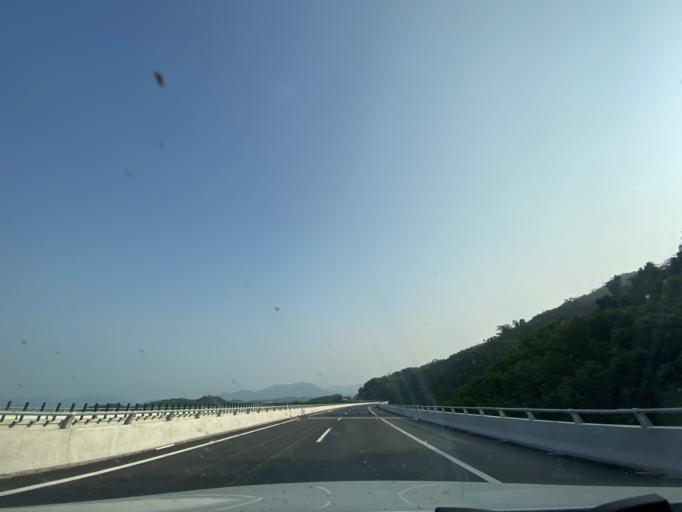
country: CN
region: Hainan
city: Xiangshui
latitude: 18.6592
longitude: 109.6290
